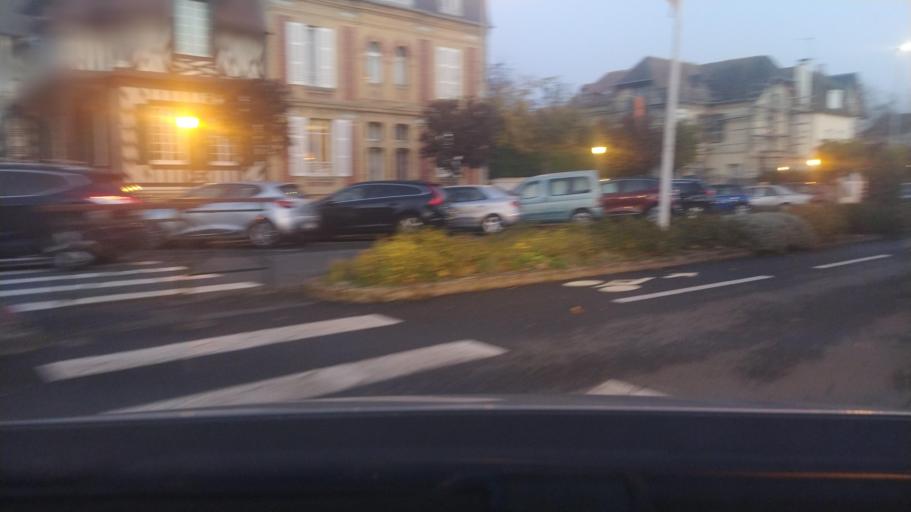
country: FR
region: Lower Normandy
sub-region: Departement du Calvados
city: Deauville
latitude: 49.3577
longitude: 0.0710
